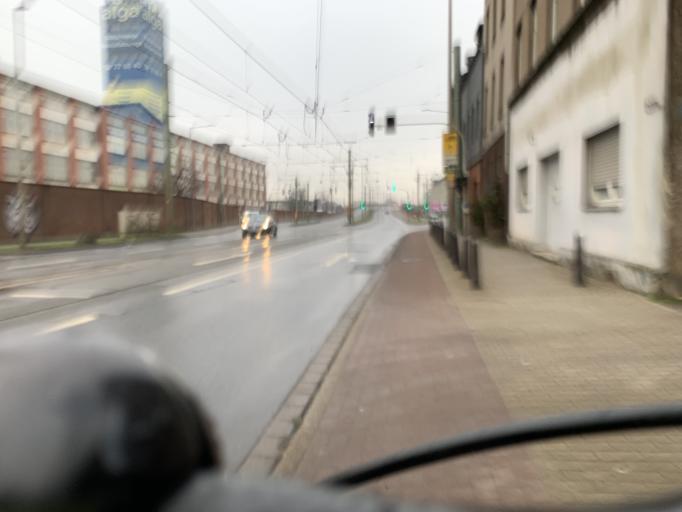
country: DE
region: North Rhine-Westphalia
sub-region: Regierungsbezirk Dusseldorf
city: Hochfeld
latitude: 51.4038
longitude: 6.7515
